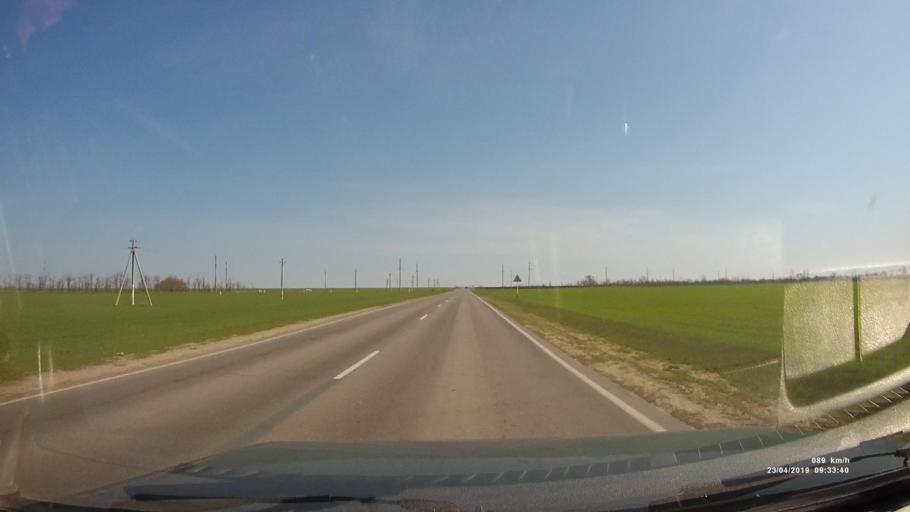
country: RU
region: Rostov
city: Gundorovskiy
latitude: 46.8035
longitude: 41.8501
